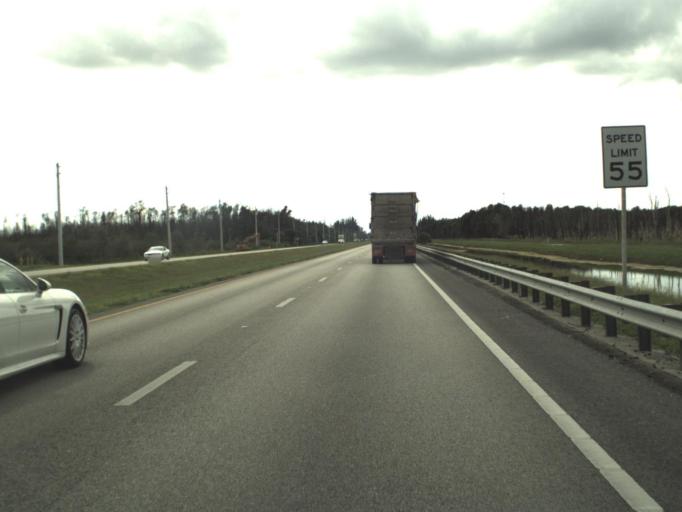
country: US
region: Florida
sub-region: Miami-Dade County
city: Tamiami
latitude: 25.7611
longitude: -80.4516
